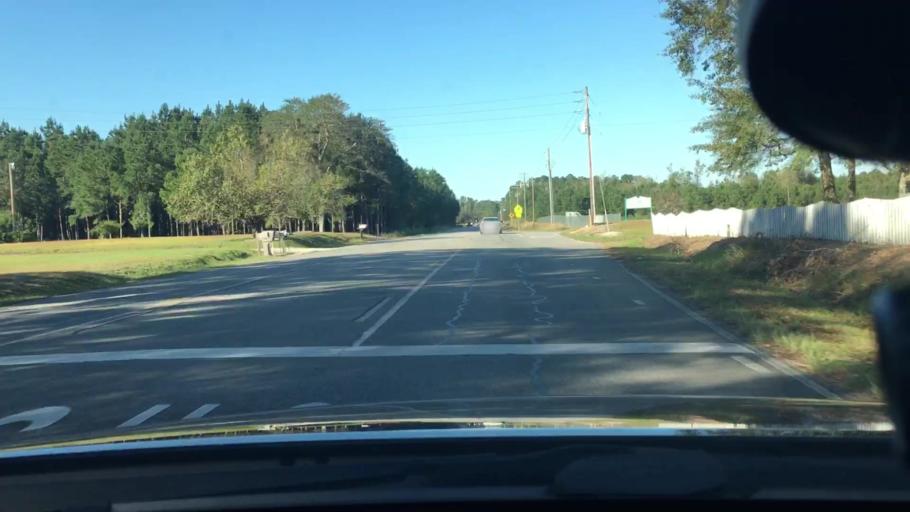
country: US
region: North Carolina
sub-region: Craven County
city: Vanceboro
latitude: 35.2322
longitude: -77.1363
